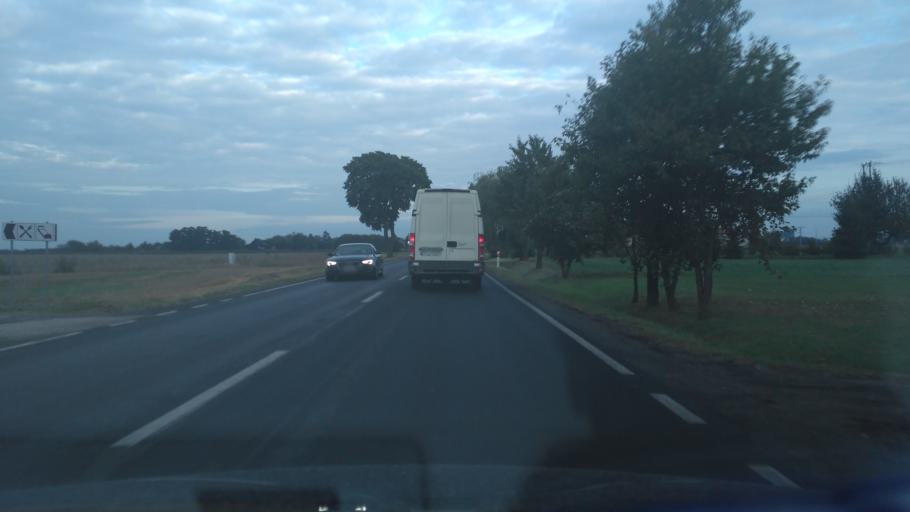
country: PL
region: Lublin Voivodeship
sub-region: Powiat leczynski
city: Spiczyn
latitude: 51.2992
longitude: 22.7641
